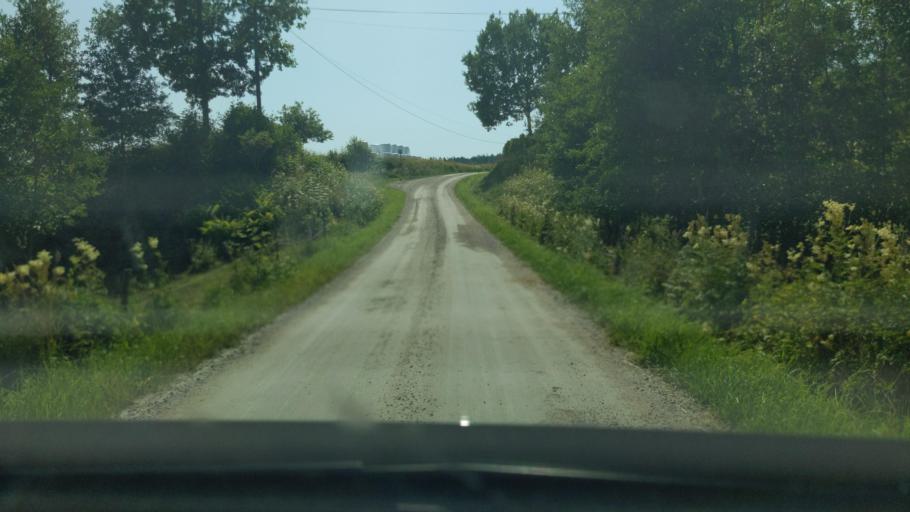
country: SE
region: Vaestra Goetaland
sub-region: Uddevalla Kommun
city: Uddevalla
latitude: 58.3369
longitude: 11.8070
